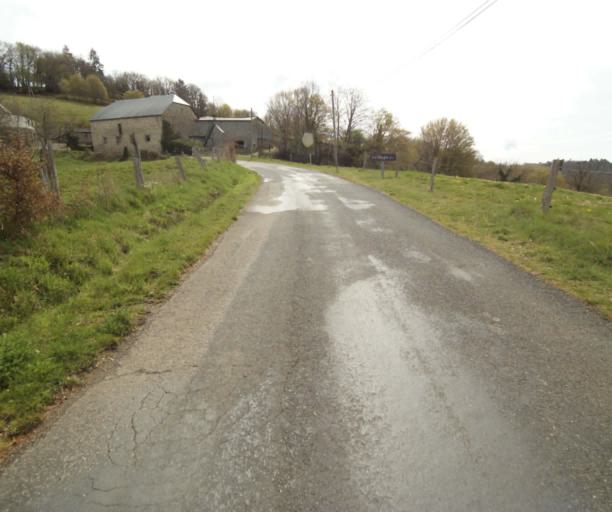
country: FR
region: Limousin
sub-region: Departement de la Correze
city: Laguenne
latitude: 45.2375
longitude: 1.8572
